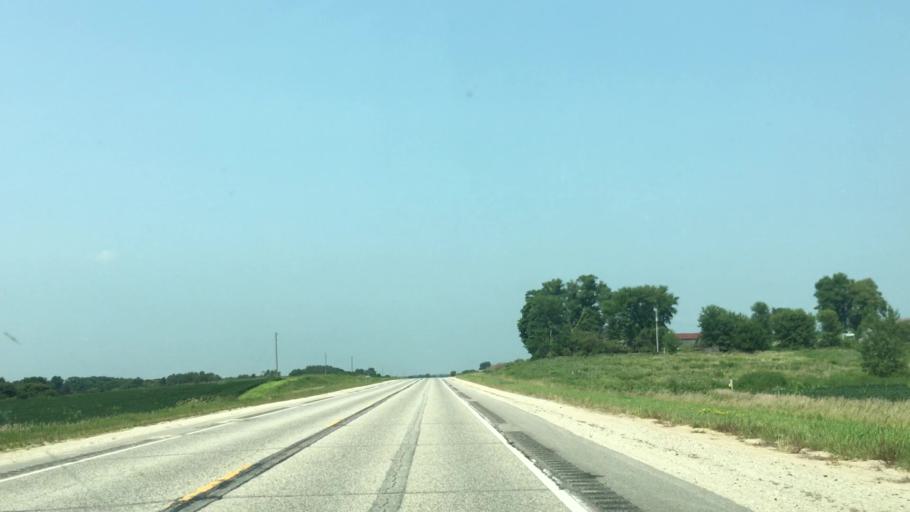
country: US
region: Iowa
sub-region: Fayette County
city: Fayette
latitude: 42.7944
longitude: -91.8050
